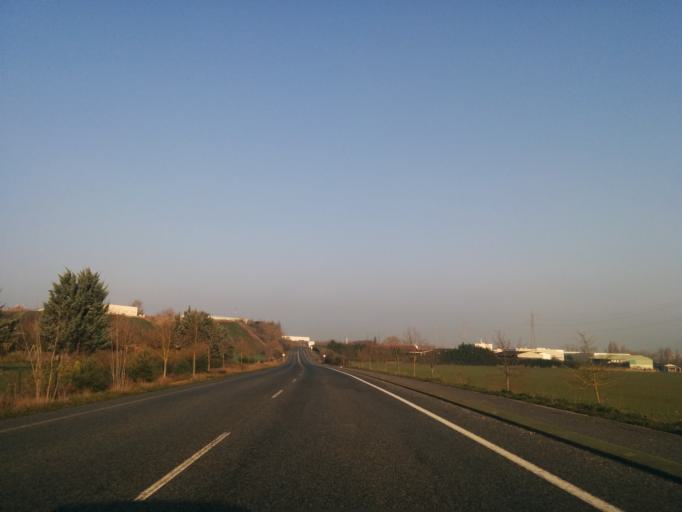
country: ES
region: Navarre
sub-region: Provincia de Navarra
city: Beriain
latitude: 42.7715
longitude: -1.6068
